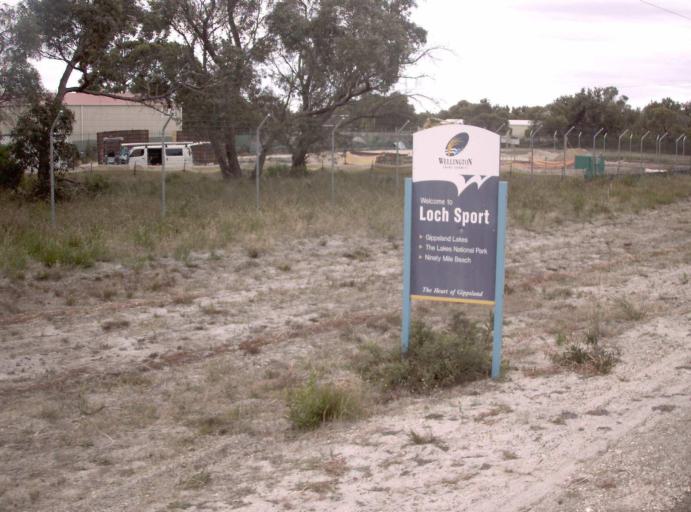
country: AU
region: Victoria
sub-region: East Gippsland
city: Bairnsdale
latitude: -38.0668
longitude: 147.5544
